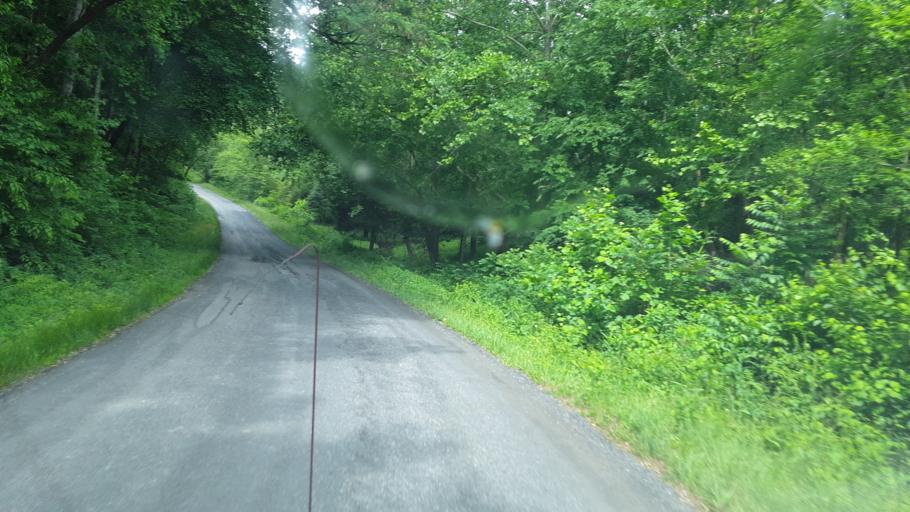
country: US
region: Virginia
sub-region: Pittsylvania County
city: Chatham
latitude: 36.8487
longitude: -79.4285
